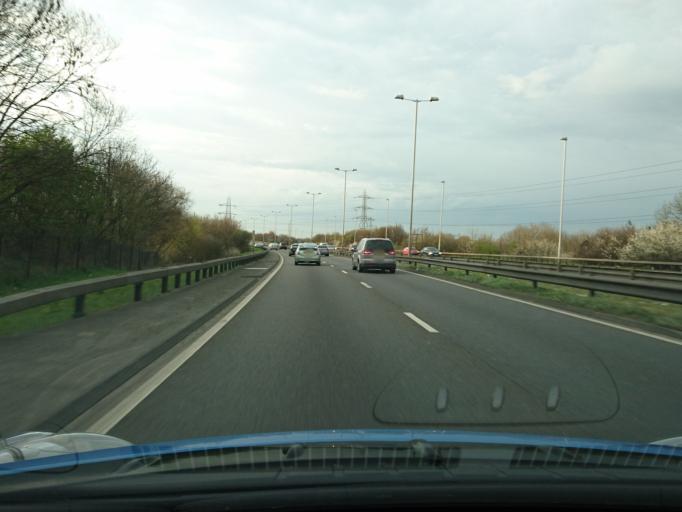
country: GB
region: England
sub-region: Greater London
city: Woodford Green
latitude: 51.5875
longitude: 0.0398
